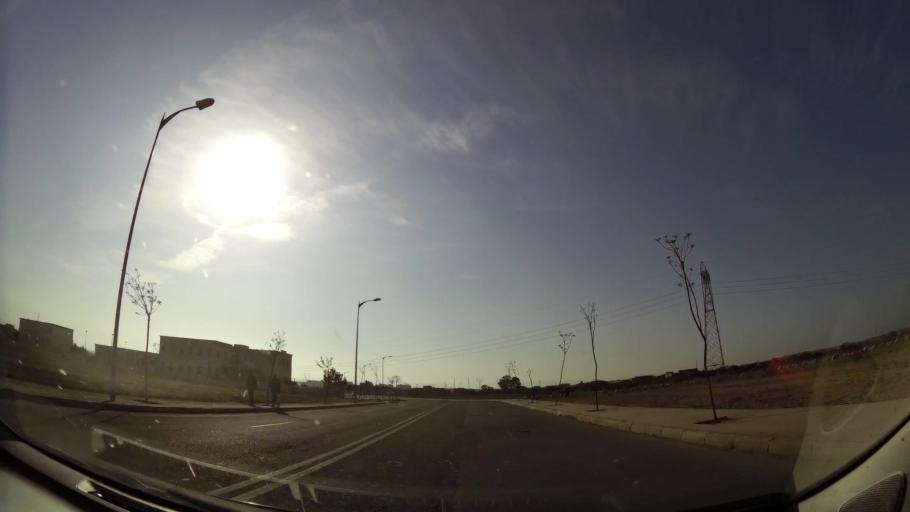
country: MA
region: Oriental
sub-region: Oujda-Angad
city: Oujda
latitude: 34.7193
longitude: -1.8998
